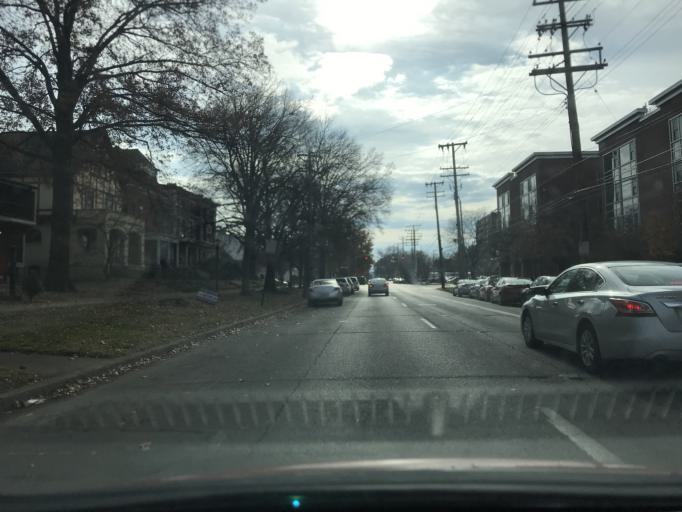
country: US
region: Kentucky
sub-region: Jefferson County
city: Louisville
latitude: 38.2214
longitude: -85.7610
